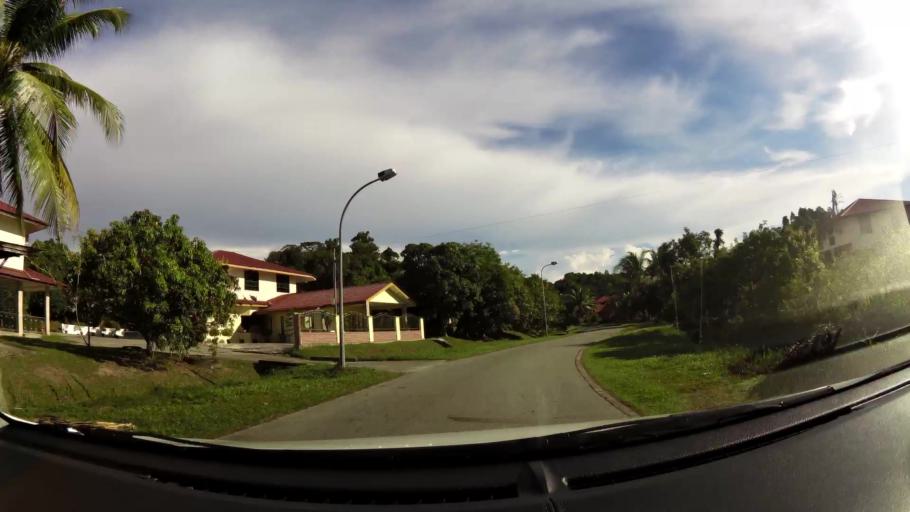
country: BN
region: Brunei and Muara
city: Bandar Seri Begawan
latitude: 4.9804
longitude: 114.9650
